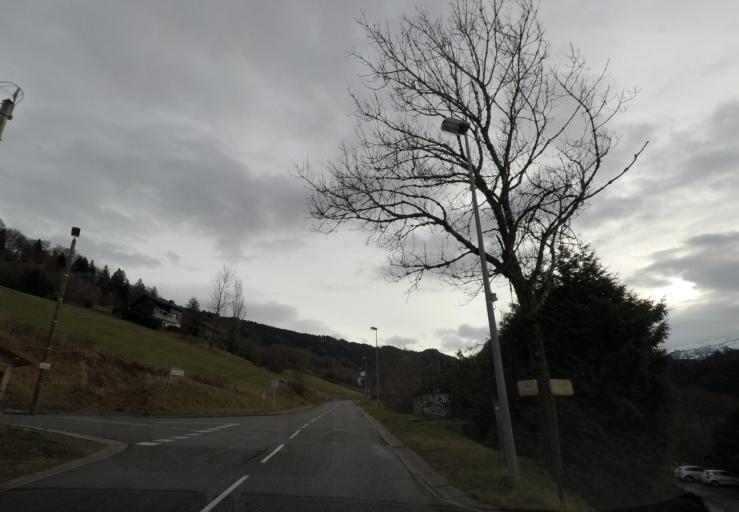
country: FR
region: Rhone-Alpes
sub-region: Departement de la Haute-Savoie
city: Chatillon-sur-Cluses
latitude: 46.0751
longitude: 6.6036
